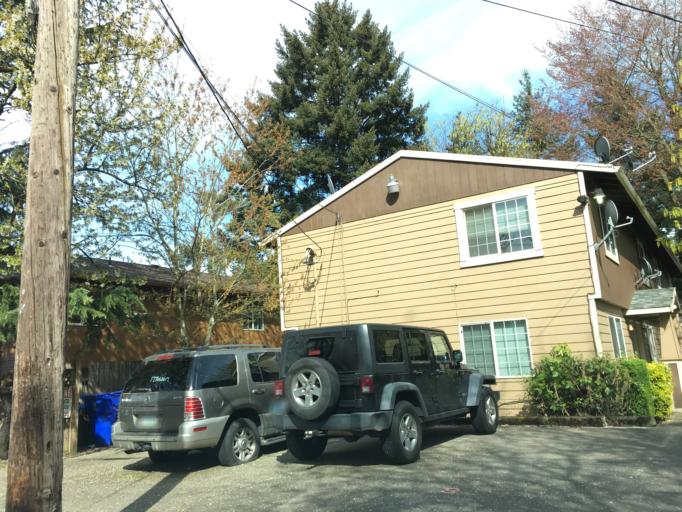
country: US
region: Oregon
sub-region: Multnomah County
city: Lents
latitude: 45.5562
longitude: -122.5399
